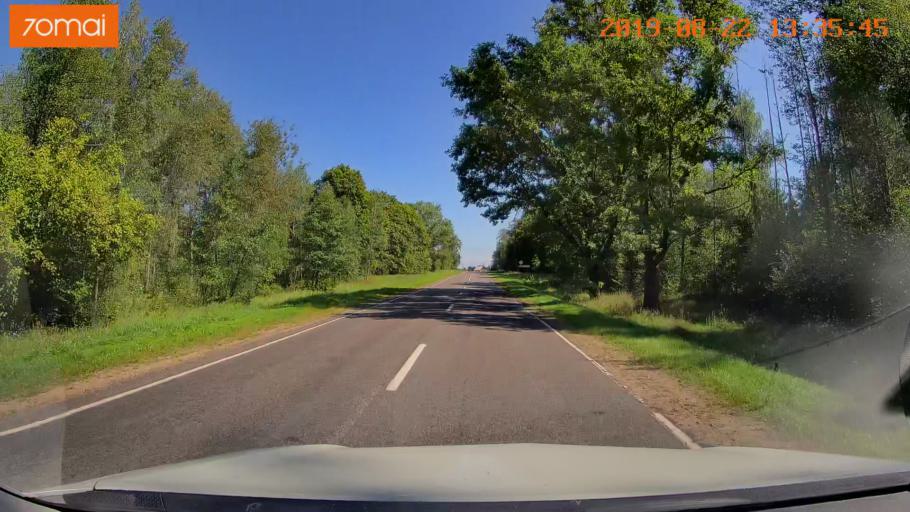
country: BY
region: Minsk
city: Staryya Darohi
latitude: 53.2131
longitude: 28.2760
